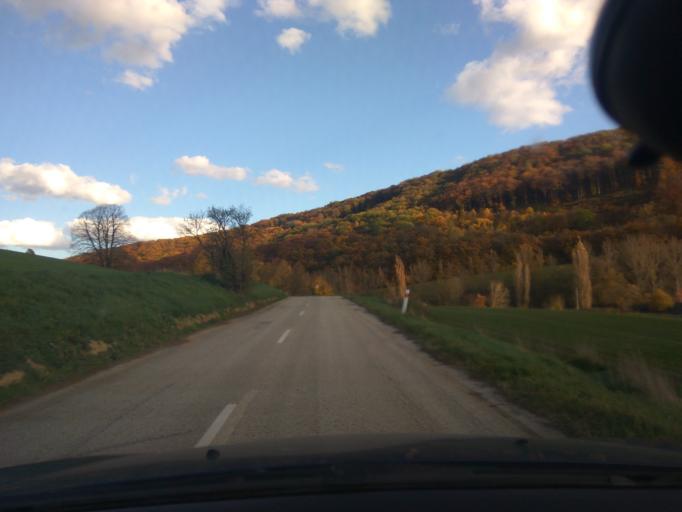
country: SK
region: Trnavsky
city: Vrbove
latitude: 48.6369
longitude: 17.6383
